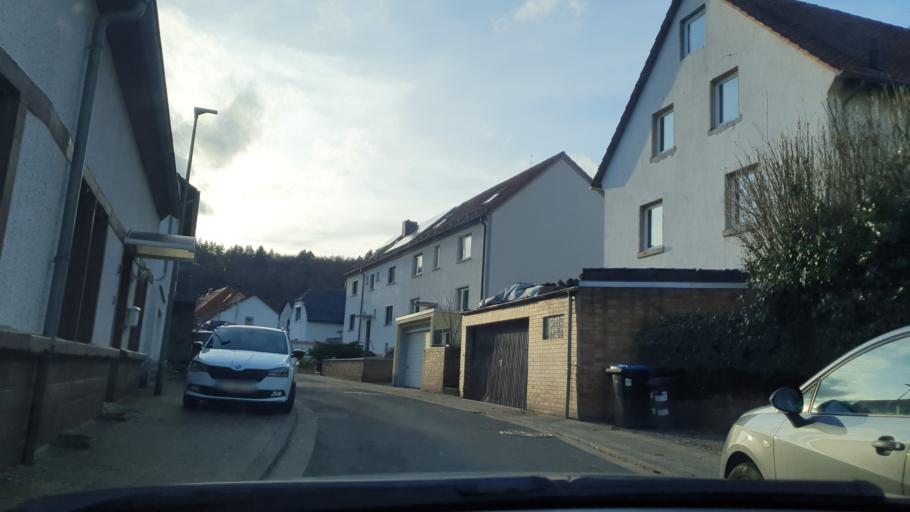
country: DE
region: Rheinland-Pfalz
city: Stelzenberg
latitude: 49.4129
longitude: 7.7018
